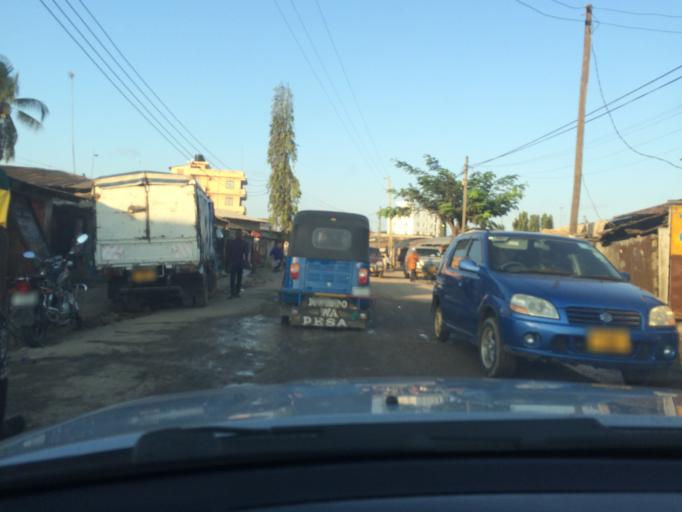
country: TZ
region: Dar es Salaam
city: Magomeni
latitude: -6.7685
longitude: 39.2672
